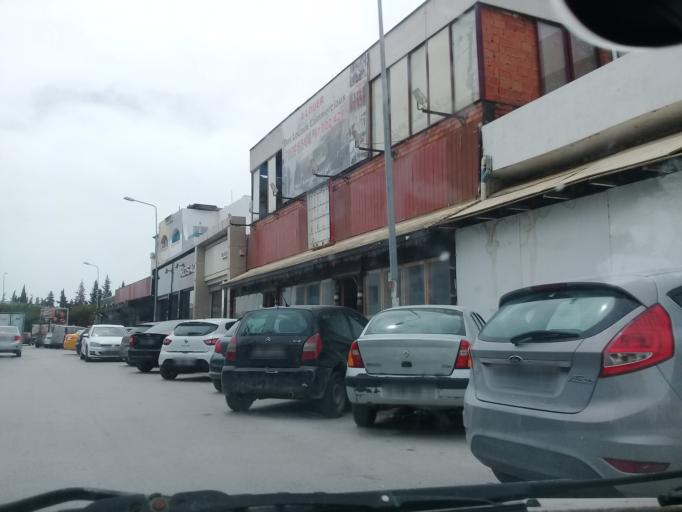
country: TN
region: Tunis
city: Tunis
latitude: 36.8366
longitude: 10.1592
